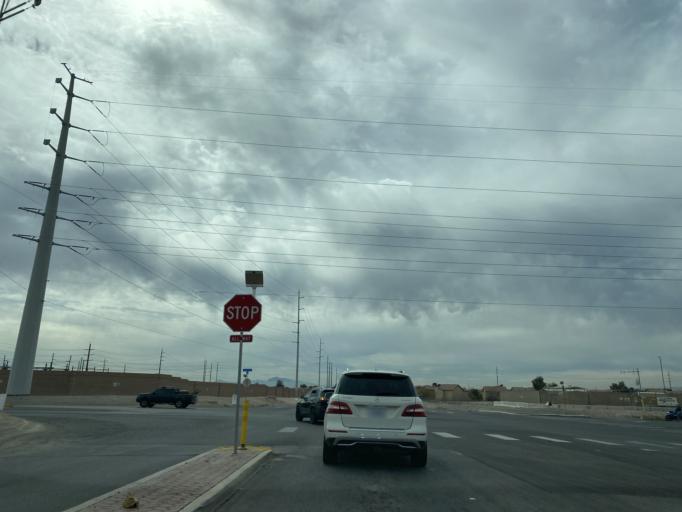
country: US
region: Nevada
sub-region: Clark County
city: Nellis Air Force Base
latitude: 36.2769
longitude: -115.0987
